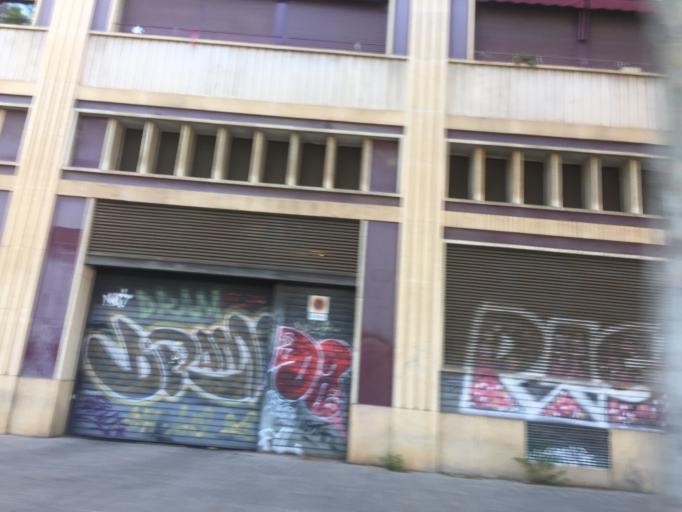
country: ES
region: Catalonia
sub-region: Provincia de Barcelona
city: Sant Marti
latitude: 41.4162
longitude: 2.1913
